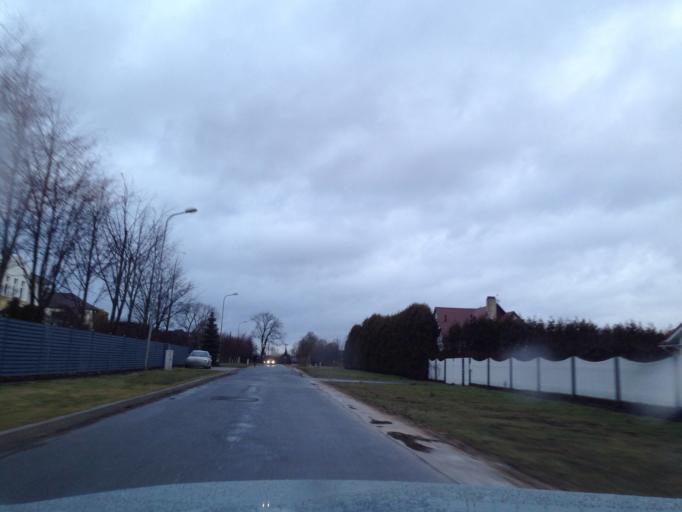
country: LV
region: Marupe
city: Marupe
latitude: 56.8902
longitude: 24.0376
